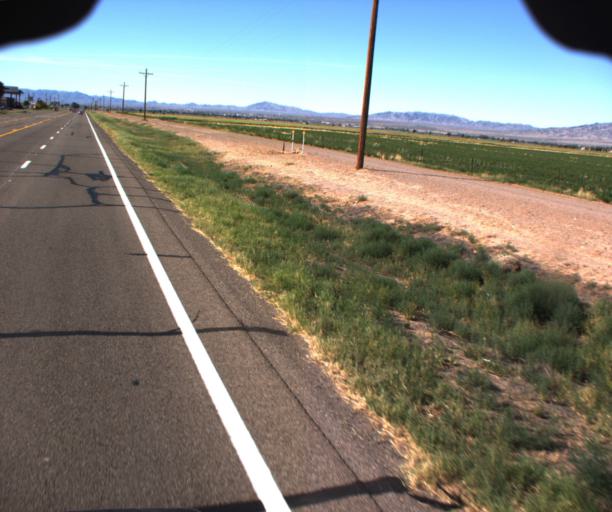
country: US
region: Arizona
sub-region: Mohave County
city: Willow Valley
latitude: 34.9018
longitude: -114.5980
